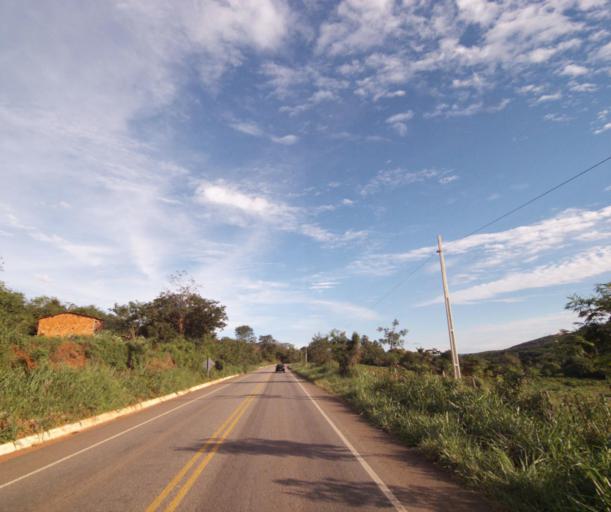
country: BR
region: Bahia
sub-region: Caetite
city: Caetite
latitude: -14.0719
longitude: -42.4587
